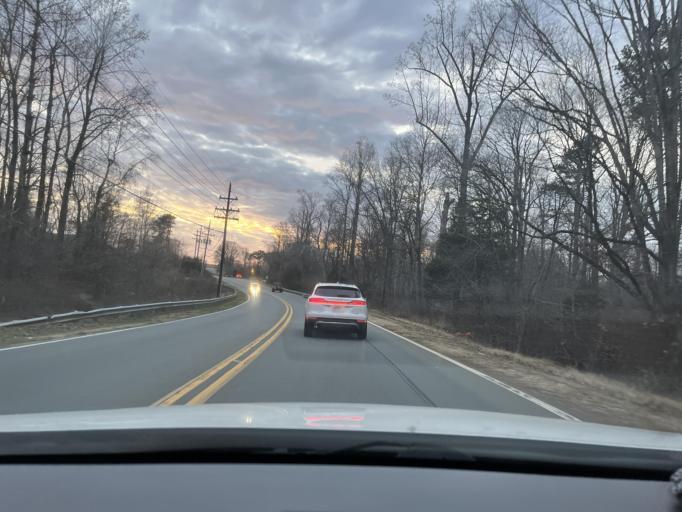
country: US
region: North Carolina
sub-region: Guilford County
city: Gibsonville
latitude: 36.0656
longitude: -79.5979
